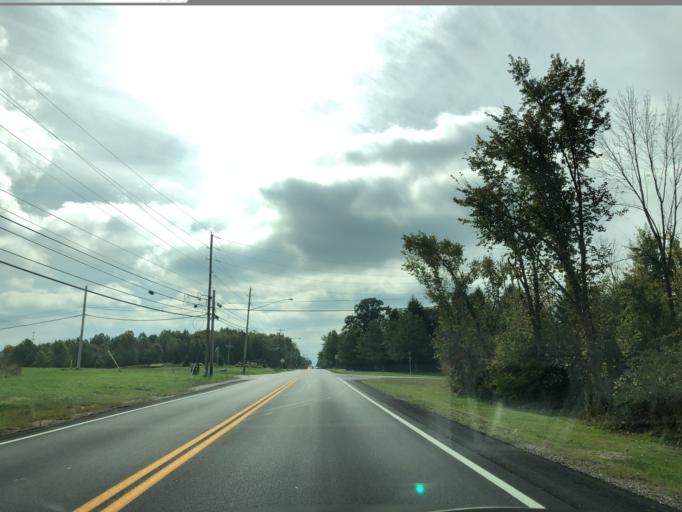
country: US
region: Ohio
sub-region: Summit County
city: Boston Heights
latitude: 41.2639
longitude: -81.5133
